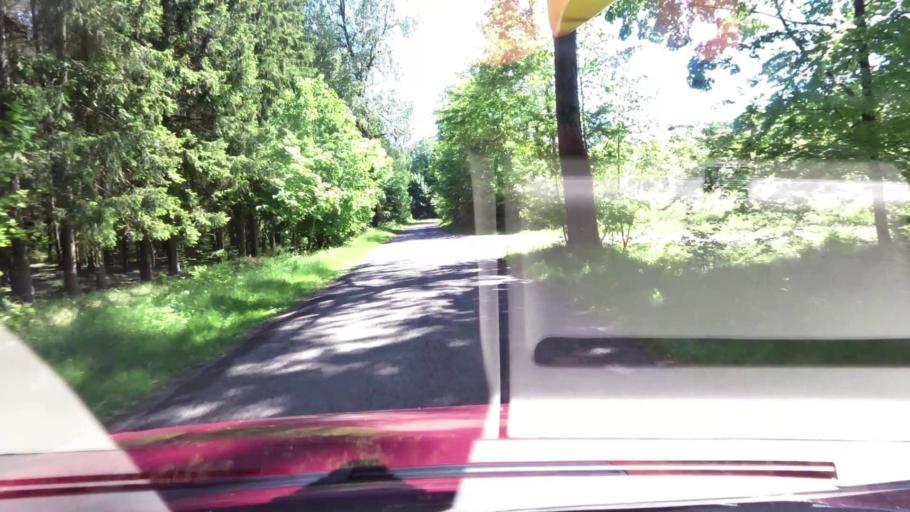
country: PL
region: West Pomeranian Voivodeship
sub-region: Powiat koszalinski
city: Bobolice
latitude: 54.0289
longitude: 16.6370
